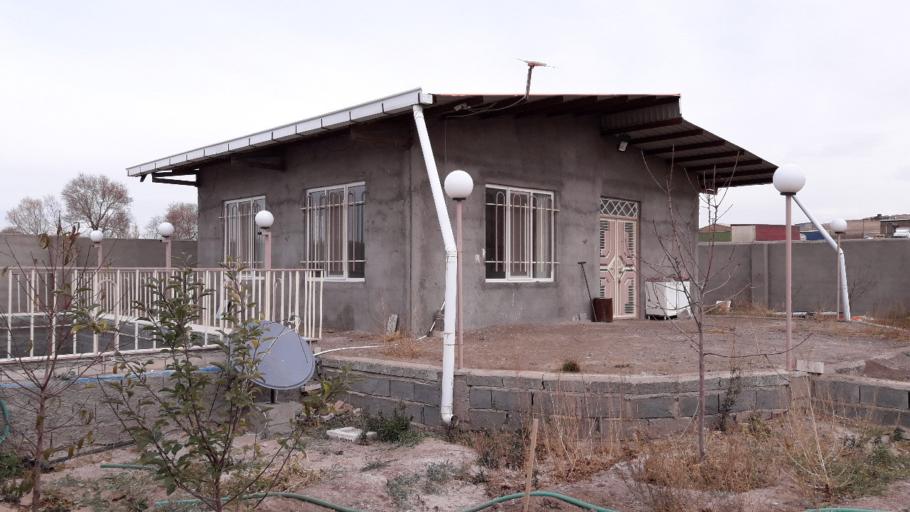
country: IR
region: East Azerbaijan
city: Bostanabad
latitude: 37.8903
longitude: 46.8670
